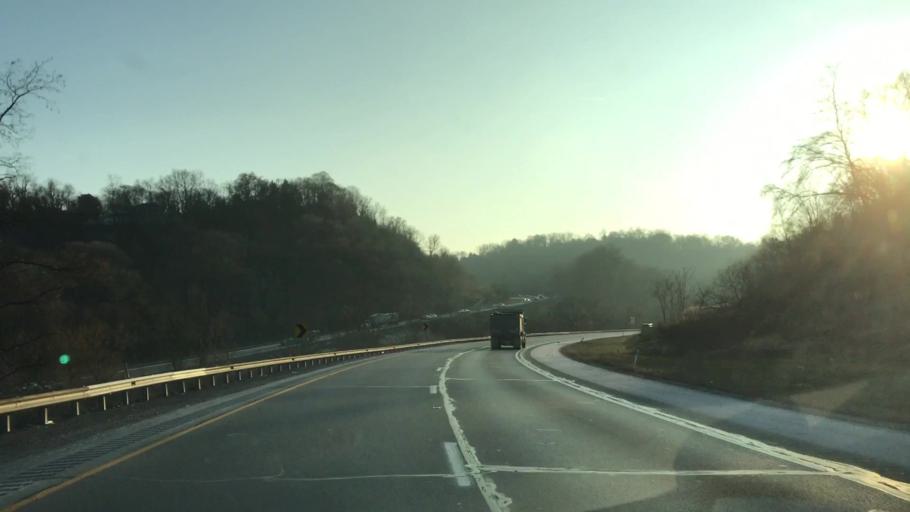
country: US
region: Pennsylvania
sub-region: Allegheny County
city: Emsworth
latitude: 40.4968
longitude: -80.1226
